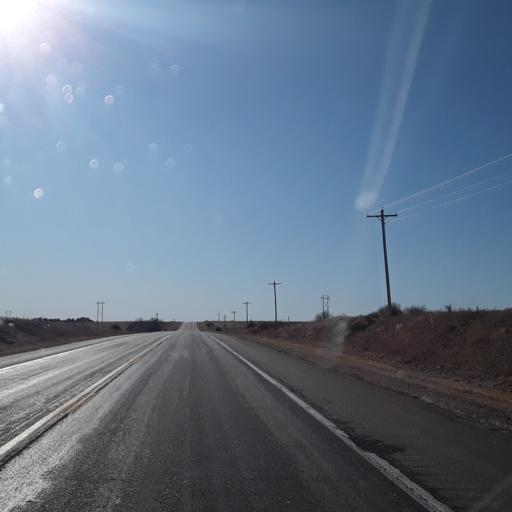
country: US
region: Nebraska
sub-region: Frontier County
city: Stockville
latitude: 40.5541
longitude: -100.6366
